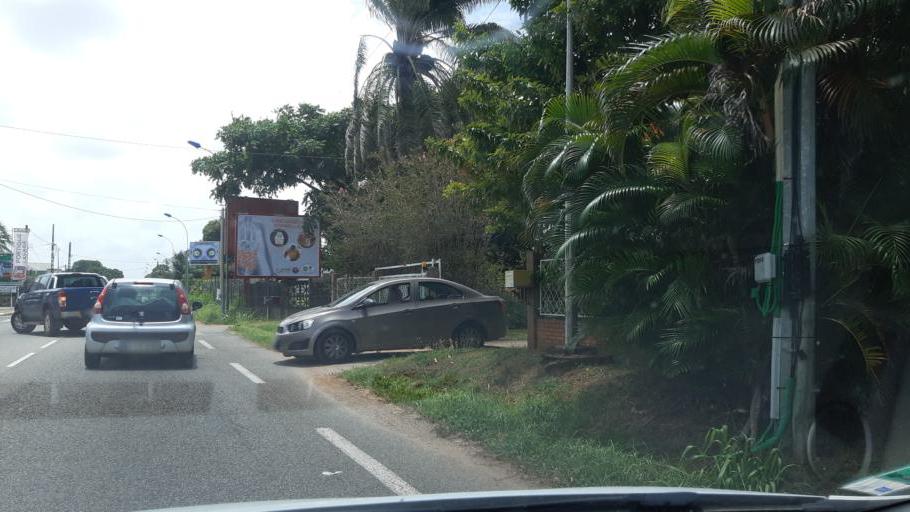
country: GF
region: Guyane
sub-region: Guyane
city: Remire-Montjoly
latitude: 4.9153
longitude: -52.2751
